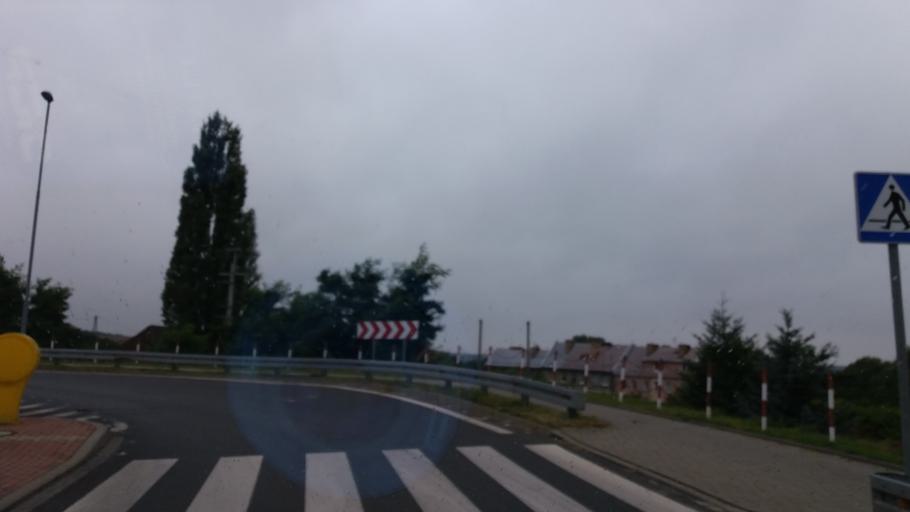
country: PL
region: West Pomeranian Voivodeship
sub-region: Powiat choszczenski
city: Choszczno
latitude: 53.1670
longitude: 15.4012
